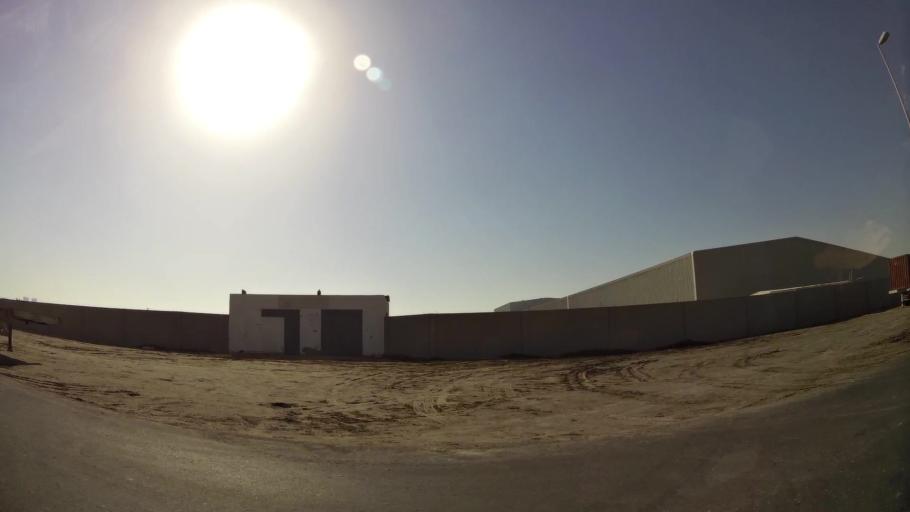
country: AE
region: Dubai
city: Dubai
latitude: 24.9898
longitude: 55.1195
